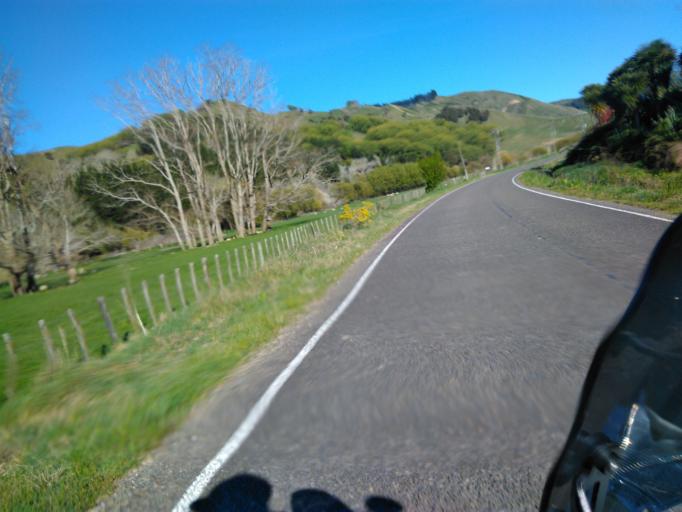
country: NZ
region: Gisborne
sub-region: Gisborne District
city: Gisborne
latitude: -38.4438
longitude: 177.7576
